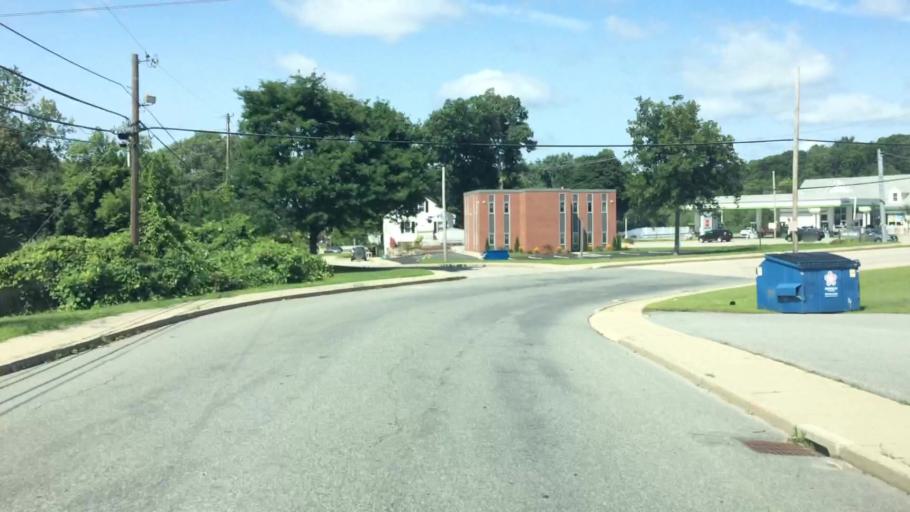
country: US
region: Rhode Island
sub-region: Providence County
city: Cumberland Hill
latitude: 41.9893
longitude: -71.4825
